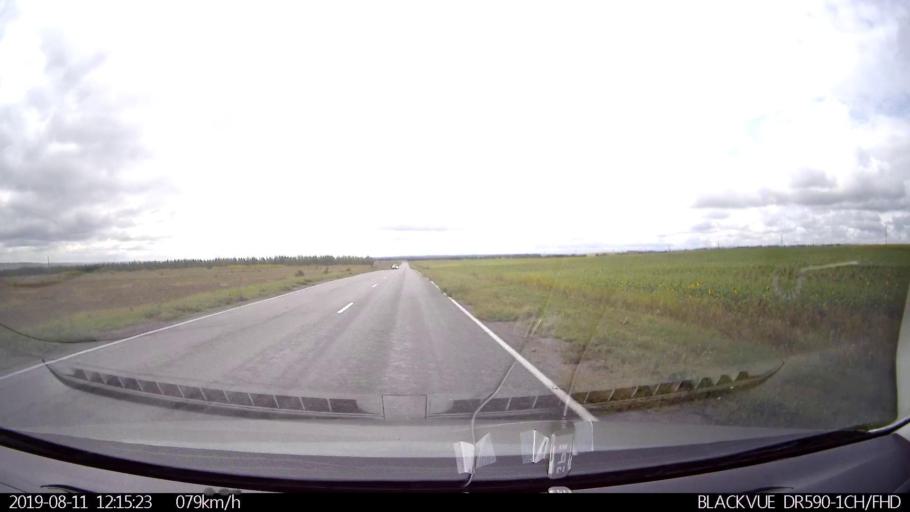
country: RU
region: Ulyanovsk
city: Ignatovka
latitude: 53.9424
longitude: 47.9691
